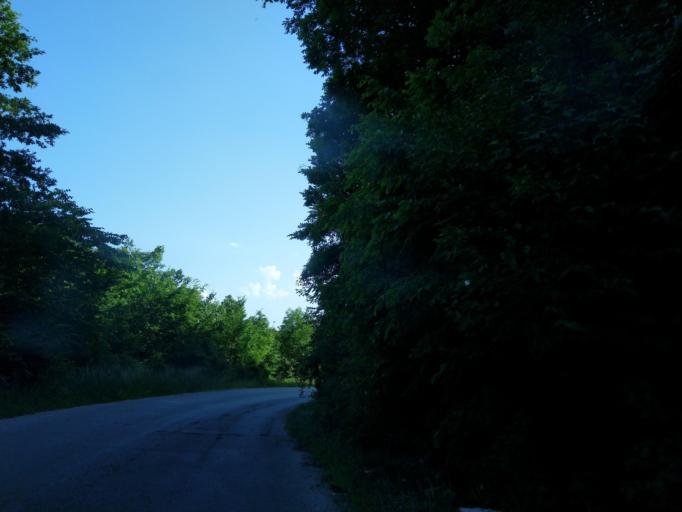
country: RS
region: Central Serbia
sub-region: Zlatiborski Okrug
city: Cajetina
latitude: 43.8641
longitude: 19.7121
